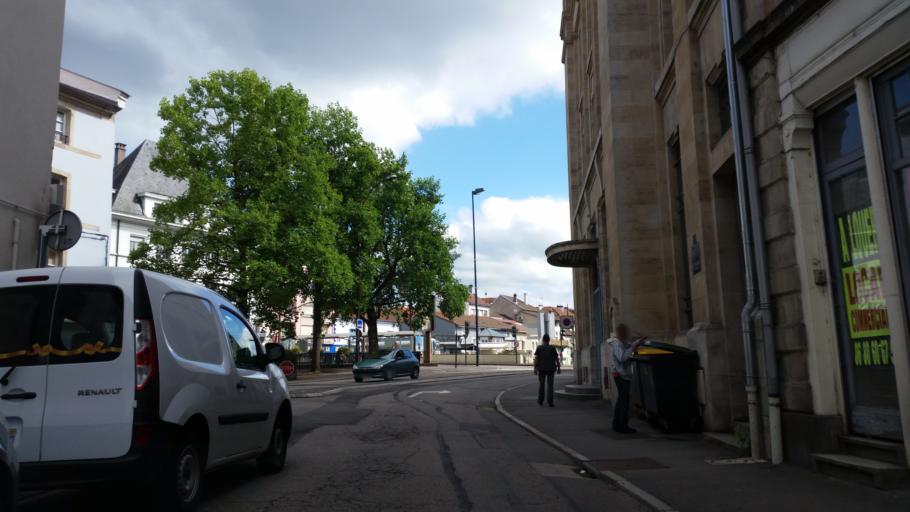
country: FR
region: Lorraine
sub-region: Departement des Vosges
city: Epinal
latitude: 48.1771
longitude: 6.4458
